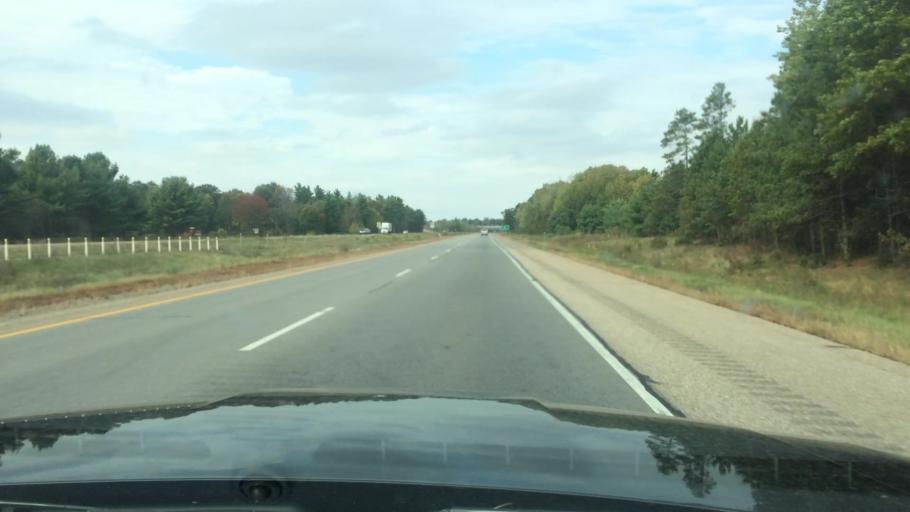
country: US
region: Wisconsin
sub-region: Marathon County
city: Mosinee
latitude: 44.7213
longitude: -89.6684
